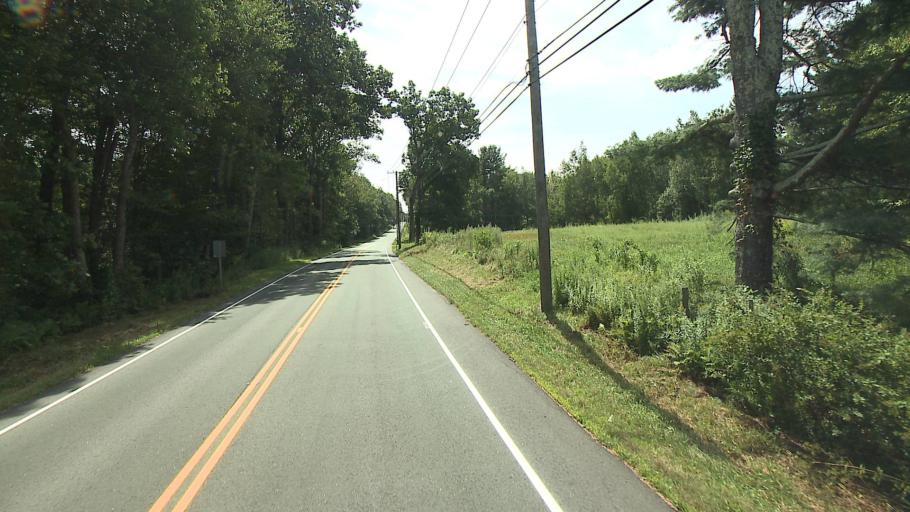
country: US
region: Connecticut
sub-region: Litchfield County
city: Bethlehem Village
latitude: 41.6262
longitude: -73.2032
